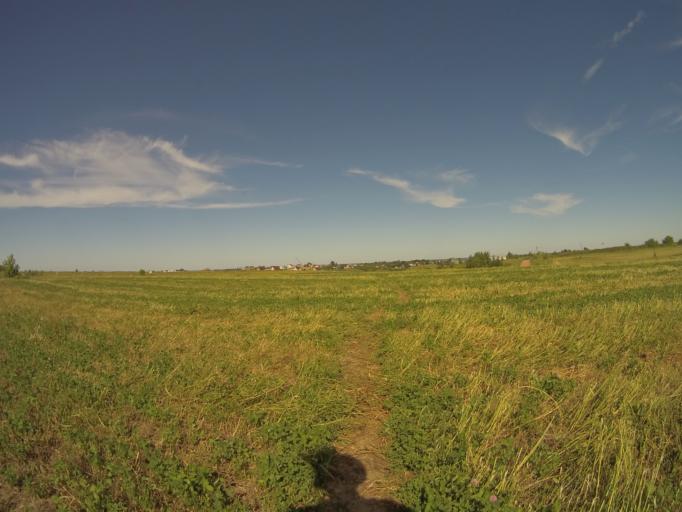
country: RU
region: Vladimir
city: Bogolyubovo
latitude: 56.2214
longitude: 40.4427
